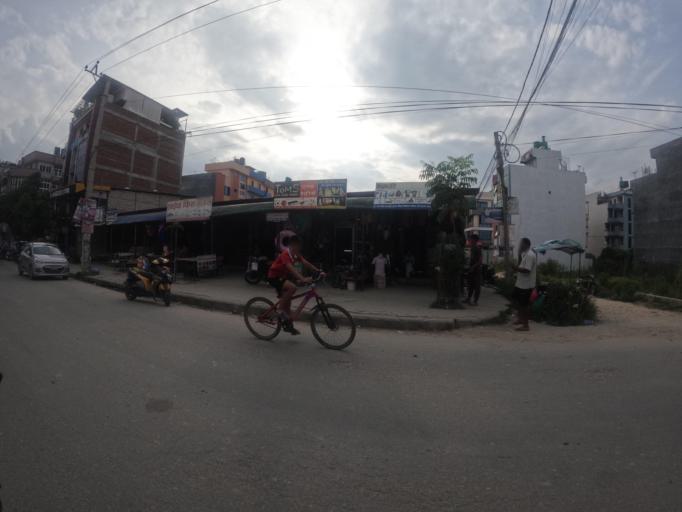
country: NP
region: Central Region
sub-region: Bagmati Zone
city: Bhaktapur
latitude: 27.6778
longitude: 85.3983
